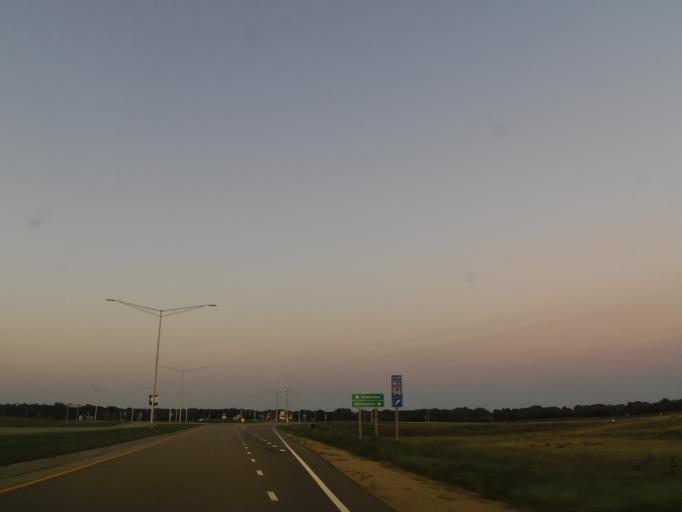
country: US
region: Minnesota
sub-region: Washington County
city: Stillwater
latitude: 45.0585
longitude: -92.7852
